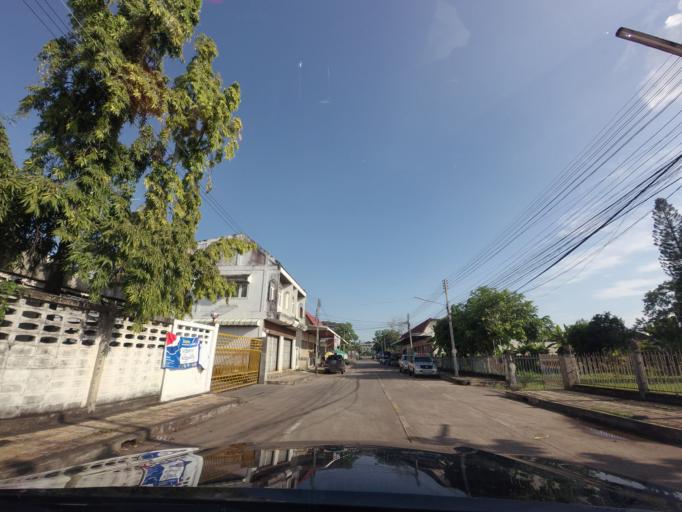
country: TH
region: Nong Khai
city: Nong Khai
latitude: 17.8822
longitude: 102.7498
